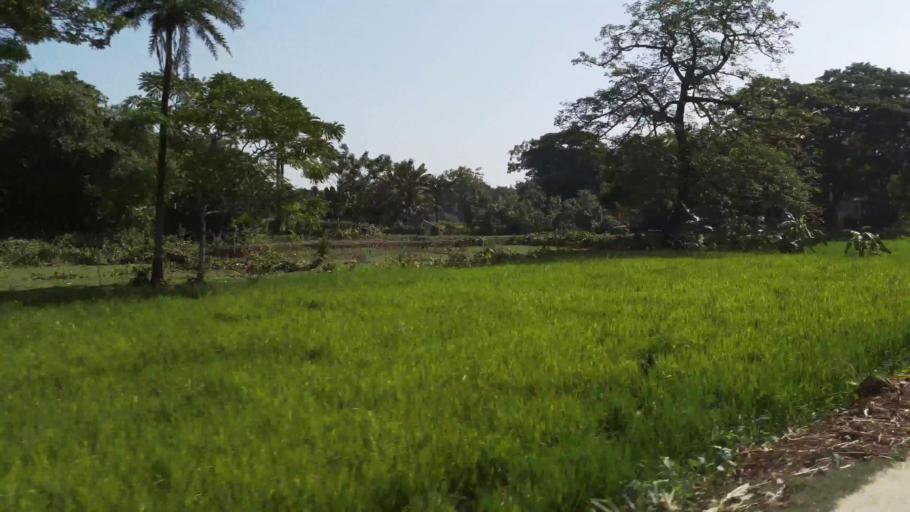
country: BD
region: Dhaka
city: Gafargaon
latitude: 24.5308
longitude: 90.5086
